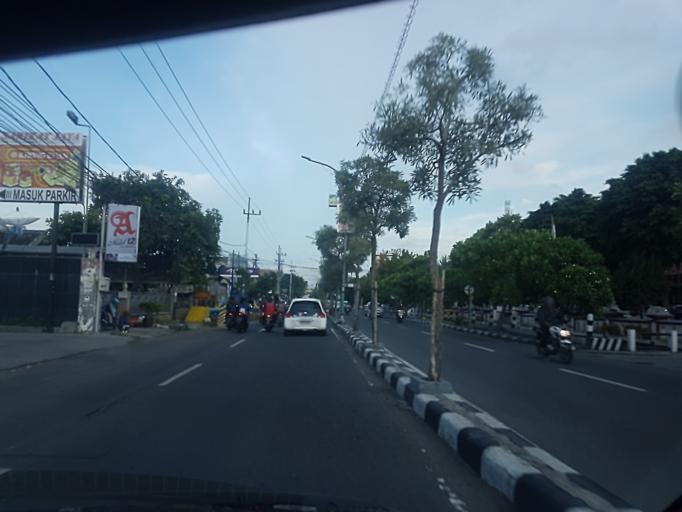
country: ID
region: East Java
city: Gresik
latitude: -7.1701
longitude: 112.6530
